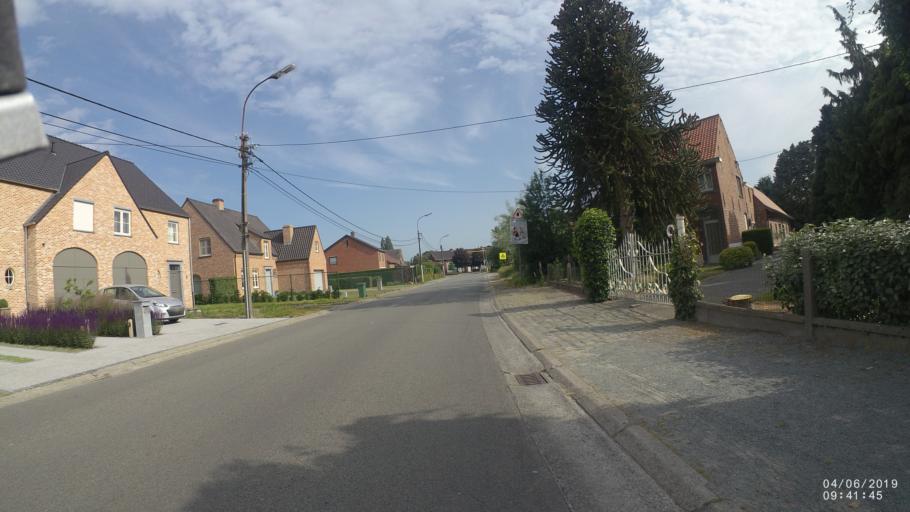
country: BE
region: Flanders
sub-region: Provincie Oost-Vlaanderen
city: Lokeren
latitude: 51.0944
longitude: 4.0068
